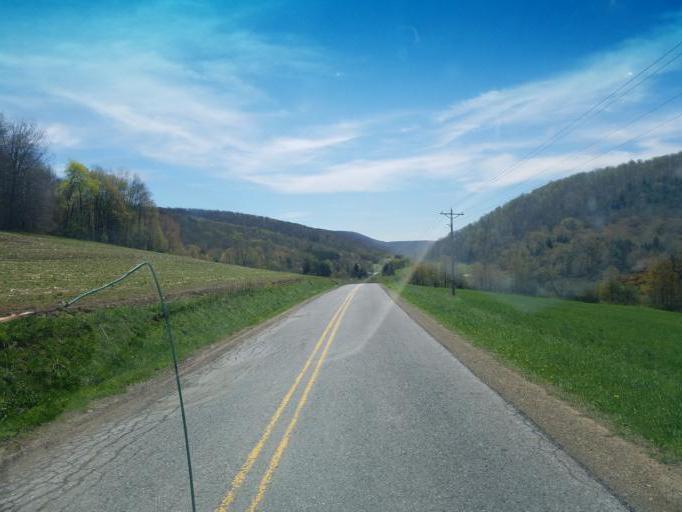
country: US
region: Pennsylvania
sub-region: Potter County
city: Galeton
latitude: 41.8800
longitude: -77.7345
